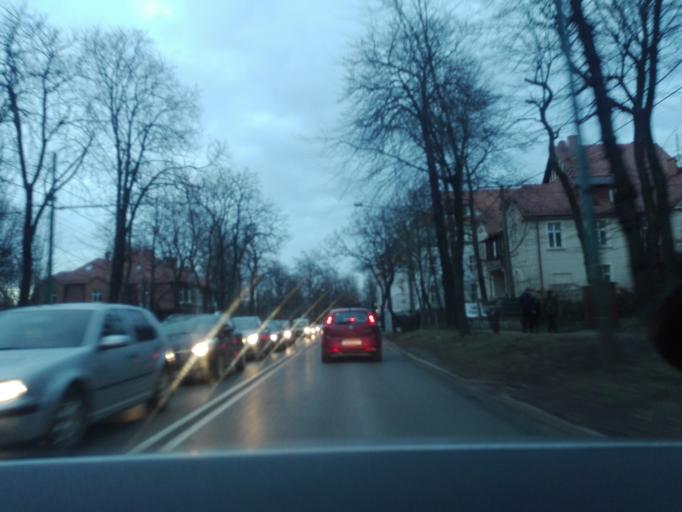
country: PL
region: Silesian Voivodeship
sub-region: Katowice
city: Katowice
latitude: 50.2766
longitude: 19.0229
